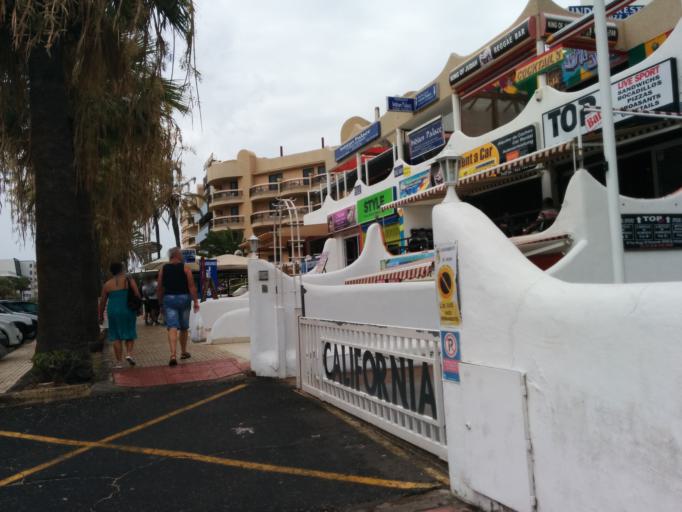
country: ES
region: Canary Islands
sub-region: Provincia de Santa Cruz de Tenerife
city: Playa de las Americas
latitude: 28.0606
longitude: -16.7287
